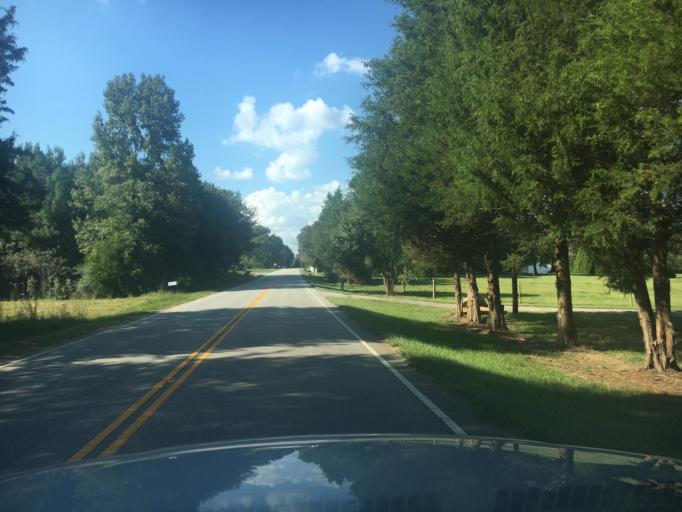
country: US
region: South Carolina
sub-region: Greenville County
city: Fountain Inn
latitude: 34.6118
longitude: -82.2349
